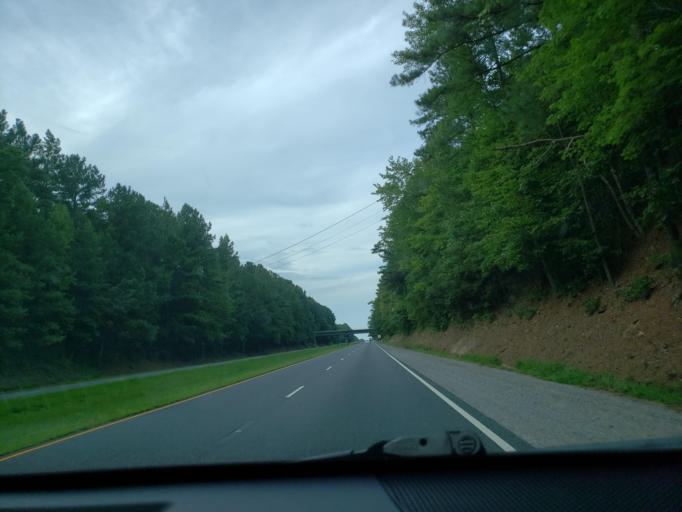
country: US
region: Virginia
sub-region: Brunswick County
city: Lawrenceville
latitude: 36.7554
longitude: -77.8328
